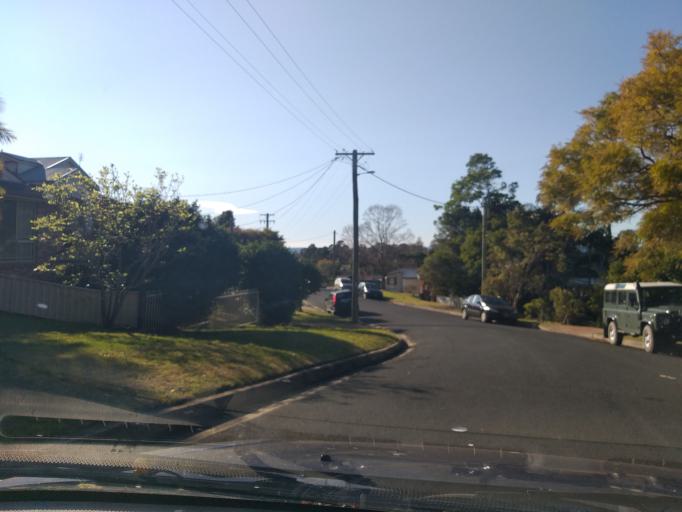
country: AU
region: New South Wales
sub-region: Wollongong
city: Bulli
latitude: -34.3187
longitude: 150.9105
